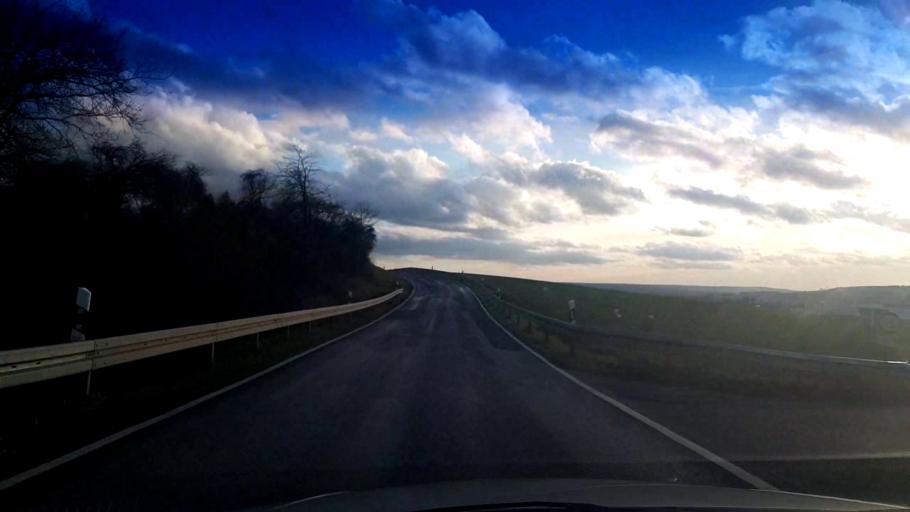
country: DE
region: Bavaria
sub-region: Upper Franconia
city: Buttenheim
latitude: 49.8139
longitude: 11.0268
